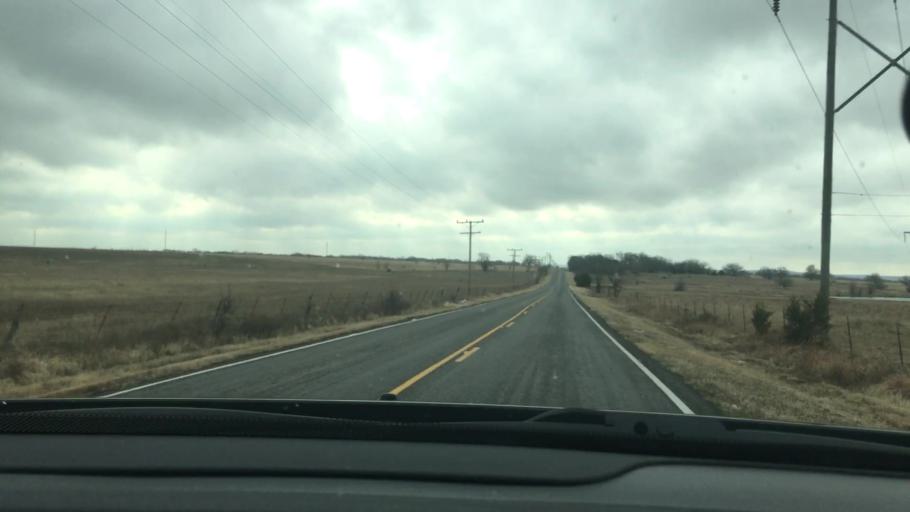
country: US
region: Oklahoma
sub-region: Bryan County
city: Durant
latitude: 34.1352
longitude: -96.4941
